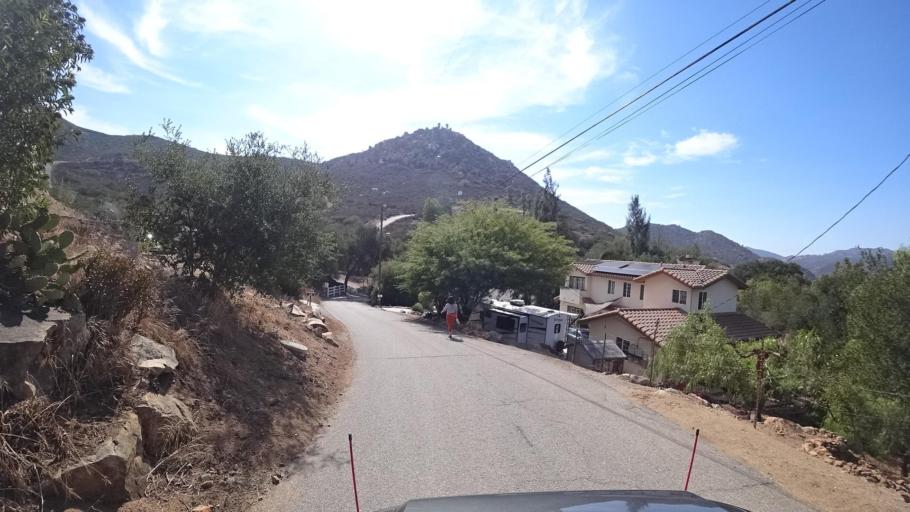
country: US
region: California
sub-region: San Diego County
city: Harbison Canyon
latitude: 32.8194
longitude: -116.8289
